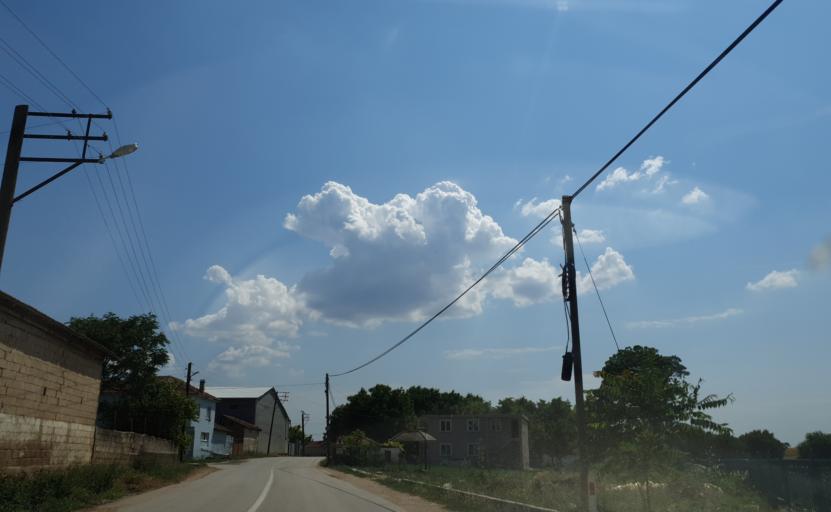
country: TR
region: Tekirdag
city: Beyazkoy
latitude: 41.4575
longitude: 27.6448
